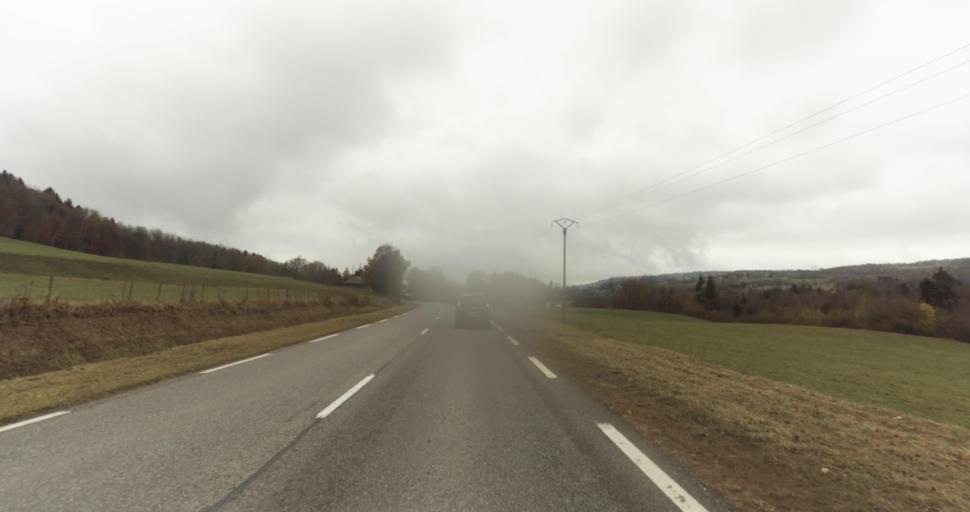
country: FR
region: Rhone-Alpes
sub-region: Departement de la Haute-Savoie
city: Evires
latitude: 46.0192
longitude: 6.2213
